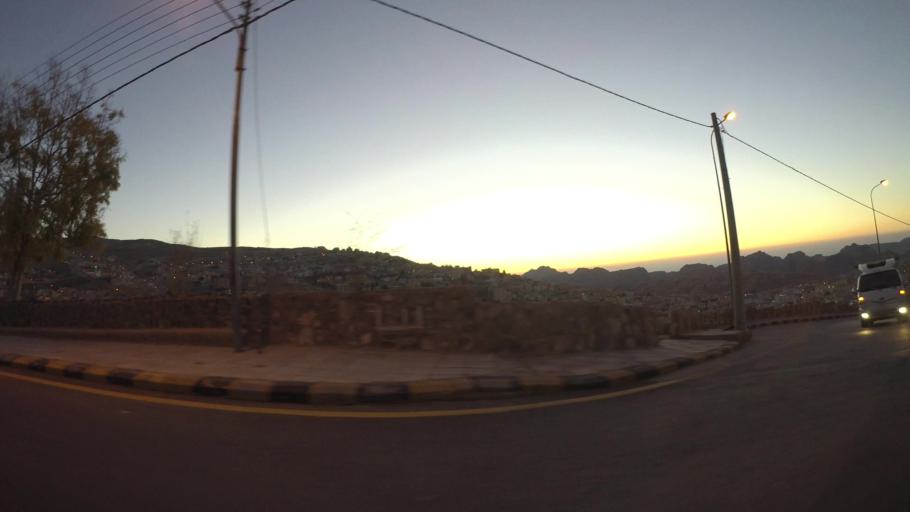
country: JO
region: Ma'an
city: Petra
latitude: 30.3204
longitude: 35.4825
